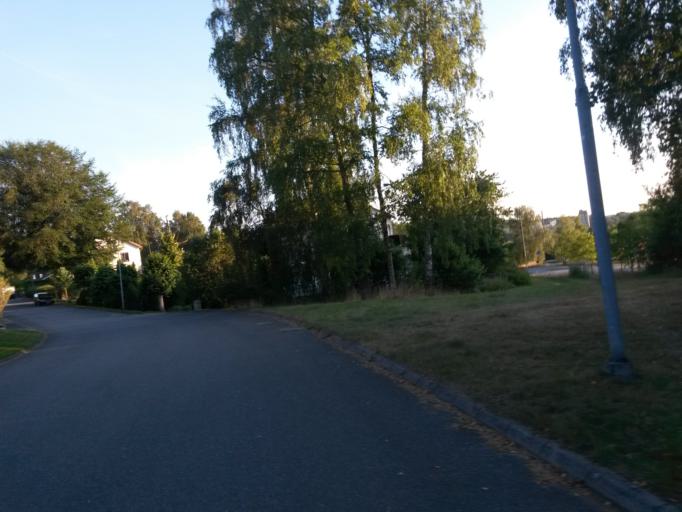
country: SE
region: Vaestra Goetaland
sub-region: Vargarda Kommun
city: Vargarda
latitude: 58.0283
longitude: 12.8012
